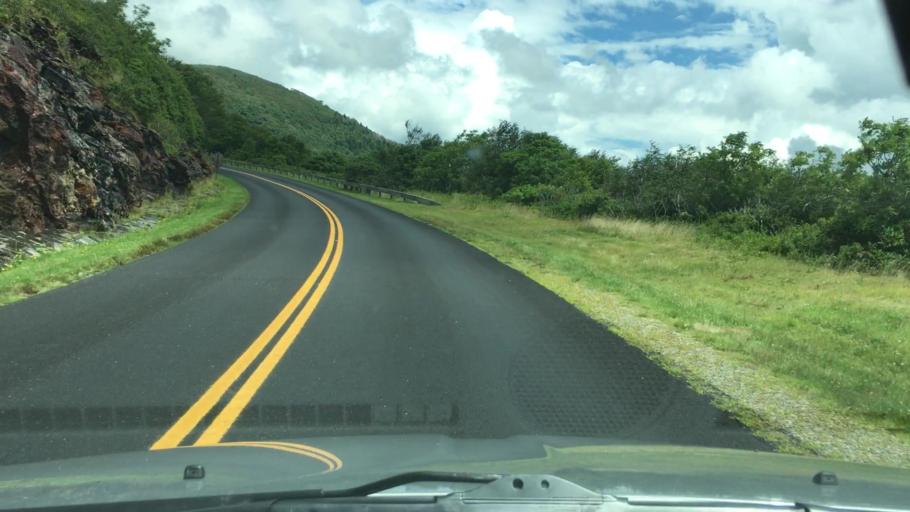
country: US
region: North Carolina
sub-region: Buncombe County
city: Black Mountain
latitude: 35.7014
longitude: -82.3759
